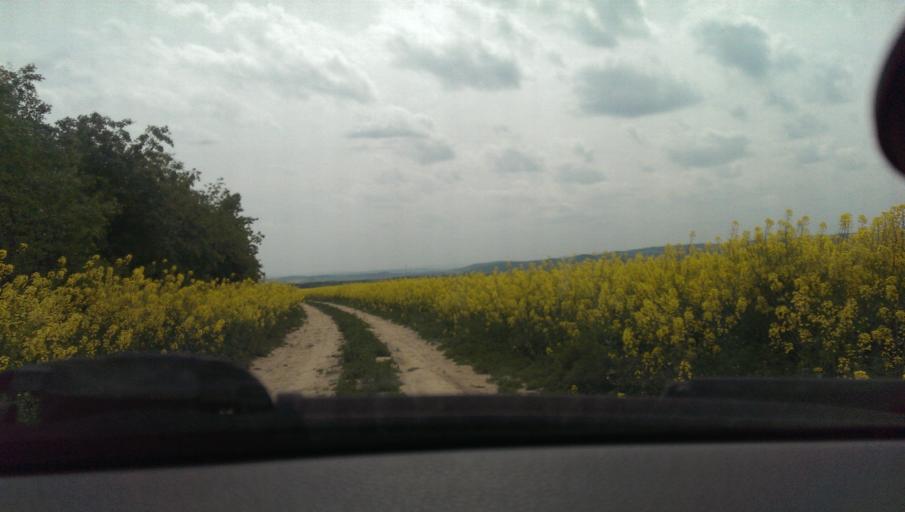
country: CZ
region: Zlin
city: Tlumacov
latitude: 49.2673
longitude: 17.5290
